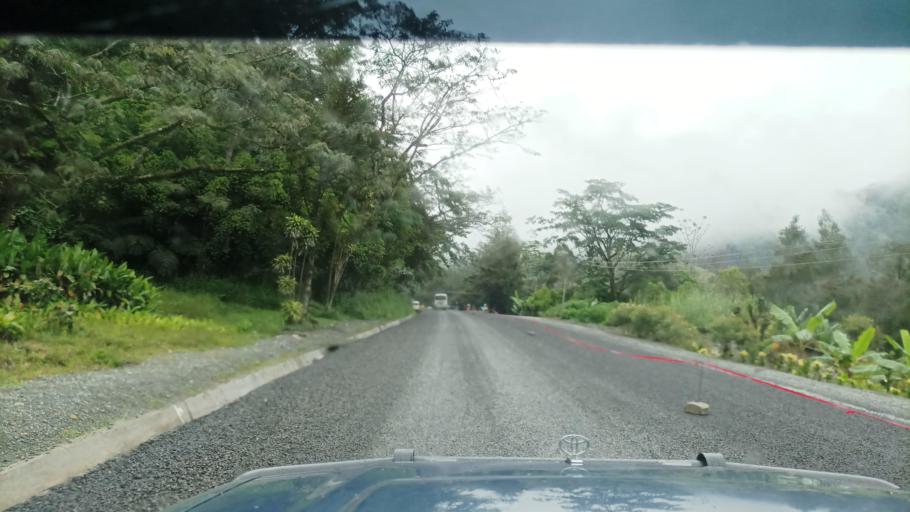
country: PG
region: Western Highlands
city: Rauna
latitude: -5.8324
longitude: 144.3631
